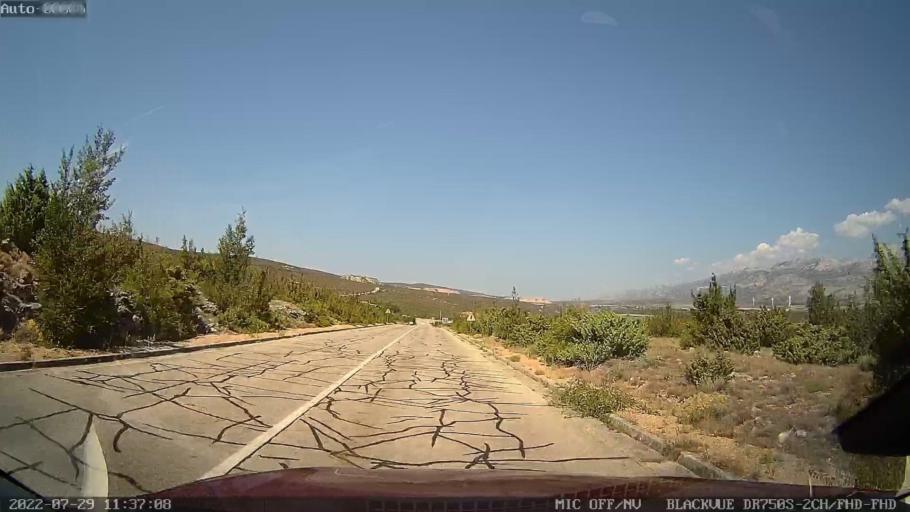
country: HR
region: Zadarska
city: Obrovac
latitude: 44.1935
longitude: 15.6871
